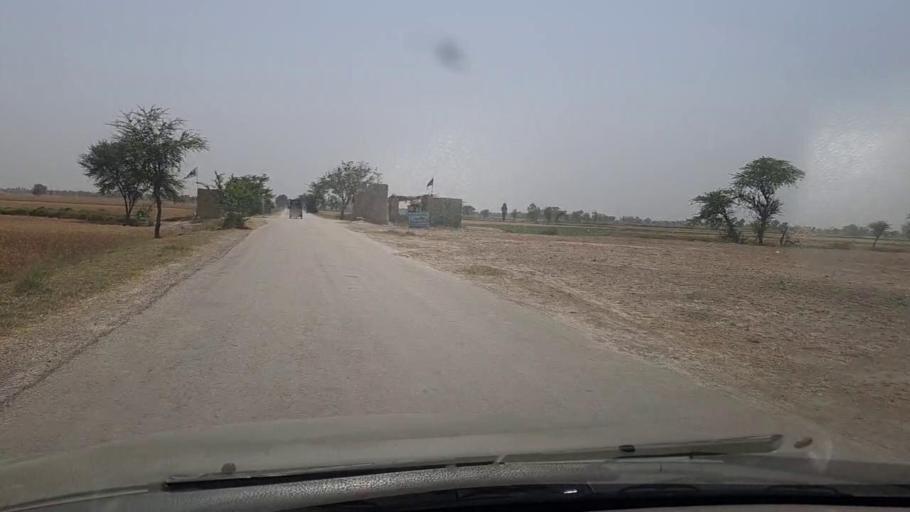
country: PK
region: Sindh
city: Miro Khan
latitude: 27.6948
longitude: 68.0585
